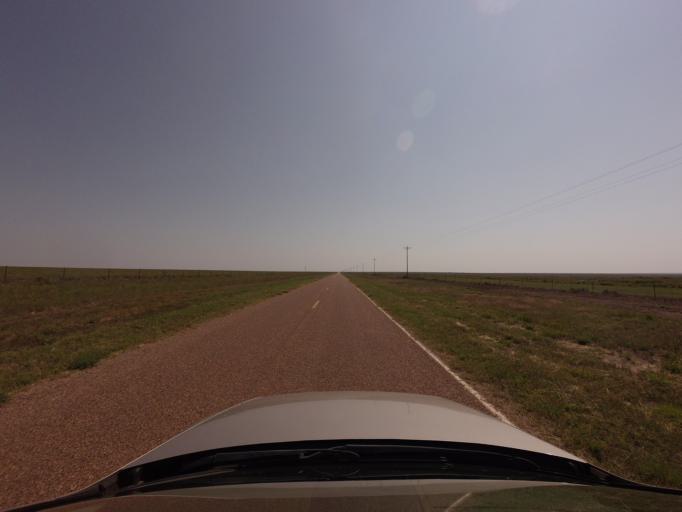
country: US
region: New Mexico
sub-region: Curry County
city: Cannon Air Force Base
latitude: 34.6330
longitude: -103.3886
